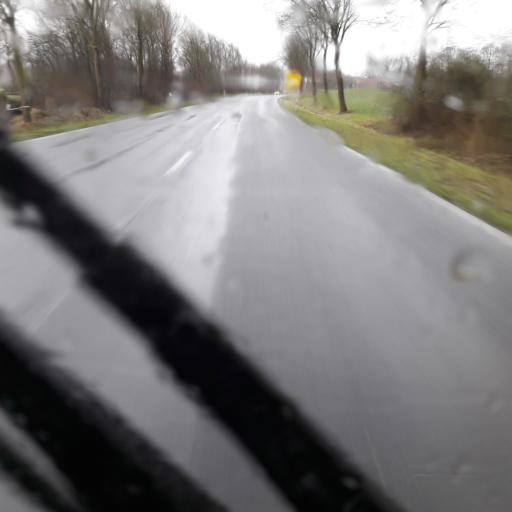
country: DE
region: North Rhine-Westphalia
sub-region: Regierungsbezirk Detmold
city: Petershagen
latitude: 52.3944
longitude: 8.9568
